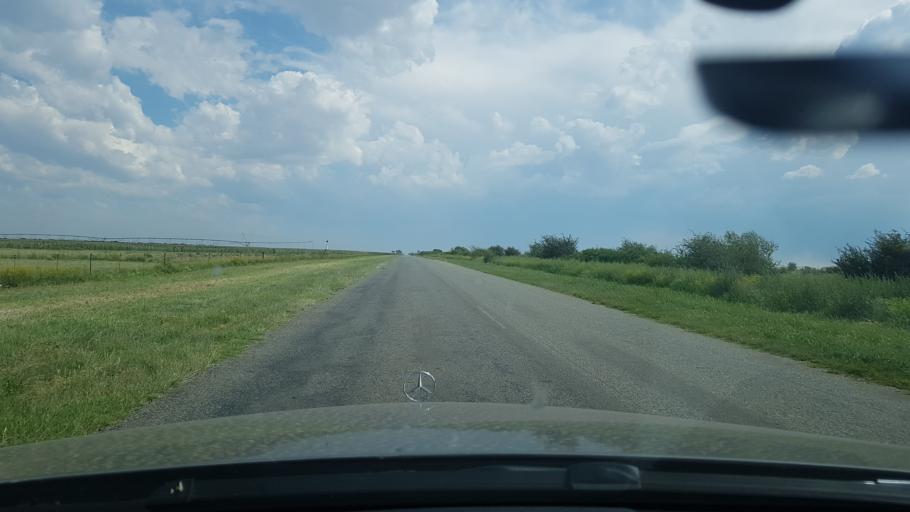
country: ZA
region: North-West
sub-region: Dr Ruth Segomotsi Mompati District Municipality
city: Bloemhof
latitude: -27.6676
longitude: 25.5917
